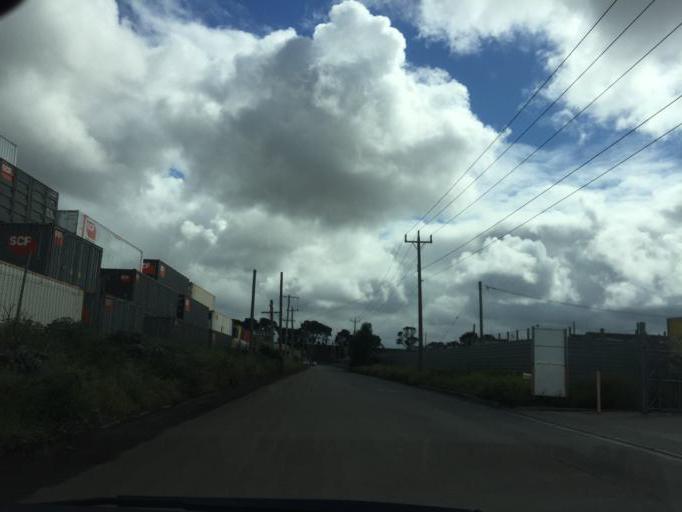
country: AU
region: Victoria
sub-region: Maribyrnong
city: Braybrook
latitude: -37.8014
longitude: 144.8531
